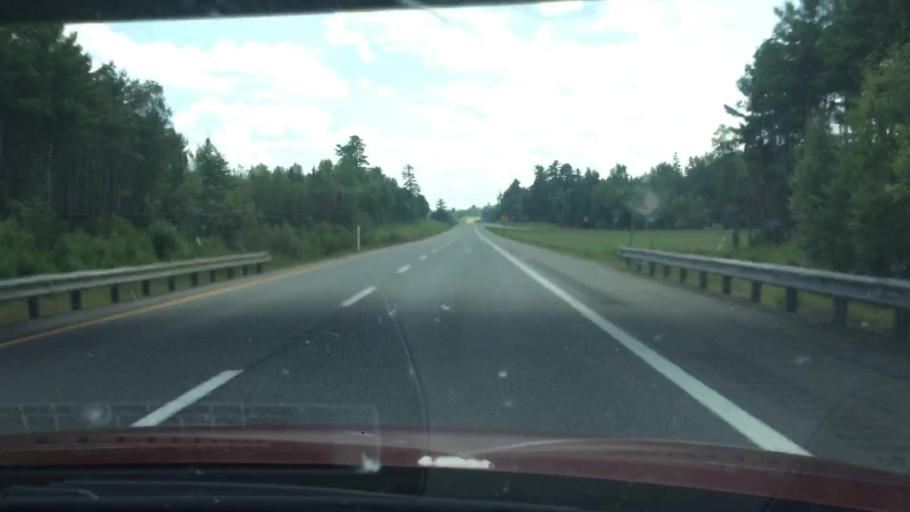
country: US
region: Maine
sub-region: Penobscot County
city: Lincoln
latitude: 45.3753
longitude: -68.6056
